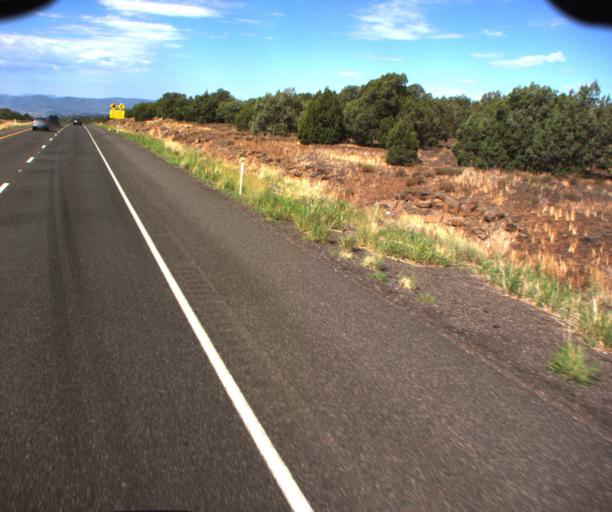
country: US
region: Arizona
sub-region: Yavapai County
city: Big Park
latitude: 34.7332
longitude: -111.7021
